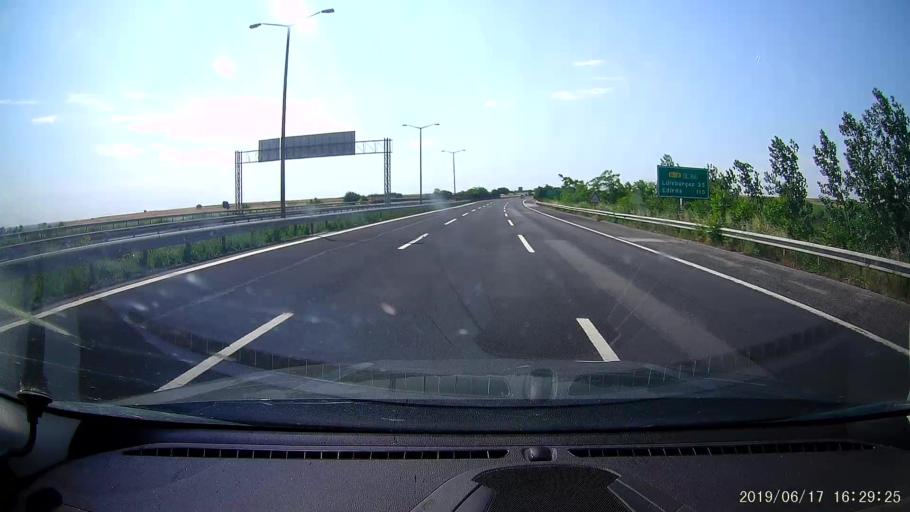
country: TR
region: Tekirdag
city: Beyazkoy
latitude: 41.3334
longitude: 27.6820
